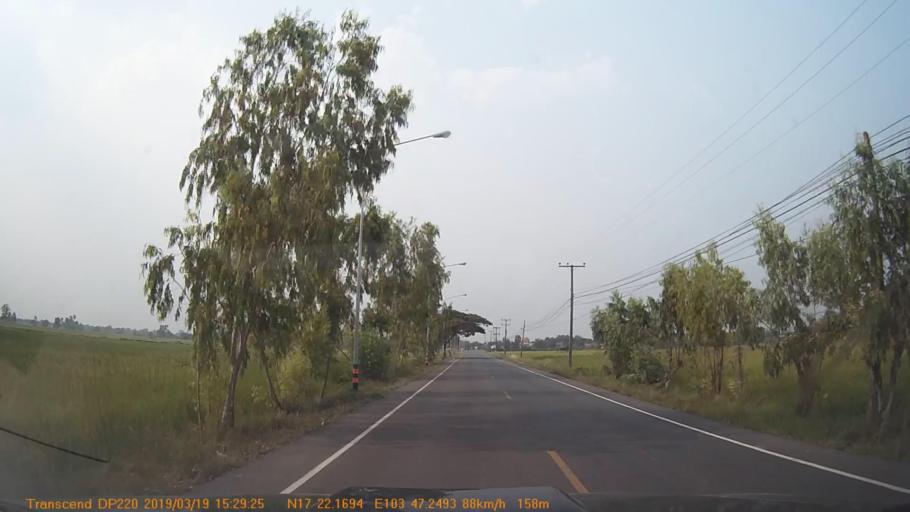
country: TH
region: Sakon Nakhon
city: Phanna Nikhom
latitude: 17.3699
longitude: 103.7874
